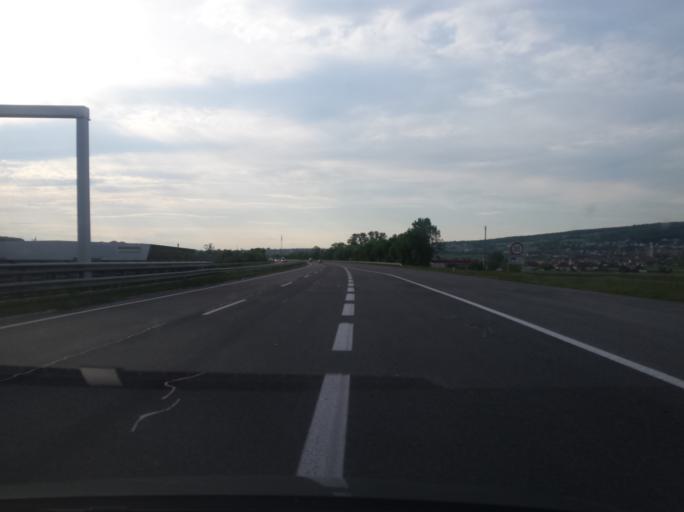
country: AT
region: Burgenland
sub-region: Eisenstadt-Umgebung
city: Wulkaprodersdorf
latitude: 47.8211
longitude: 16.4891
